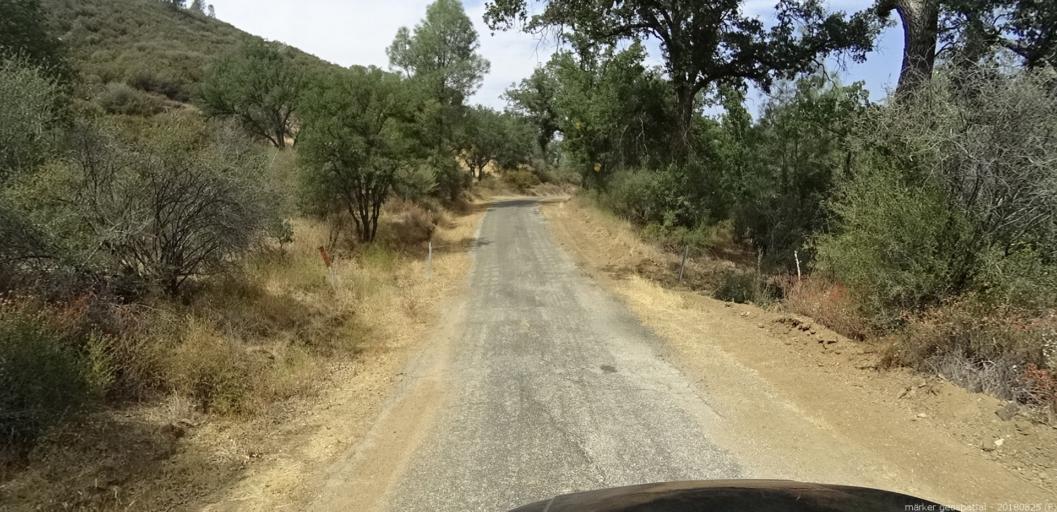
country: US
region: California
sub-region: Fresno County
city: Coalinga
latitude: 36.2224
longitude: -120.7072
